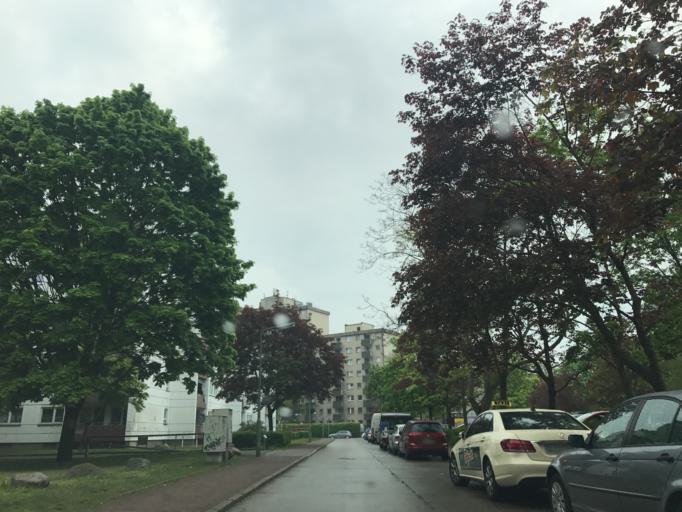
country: DE
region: Berlin
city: Staaken
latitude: 52.5483
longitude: 13.1534
